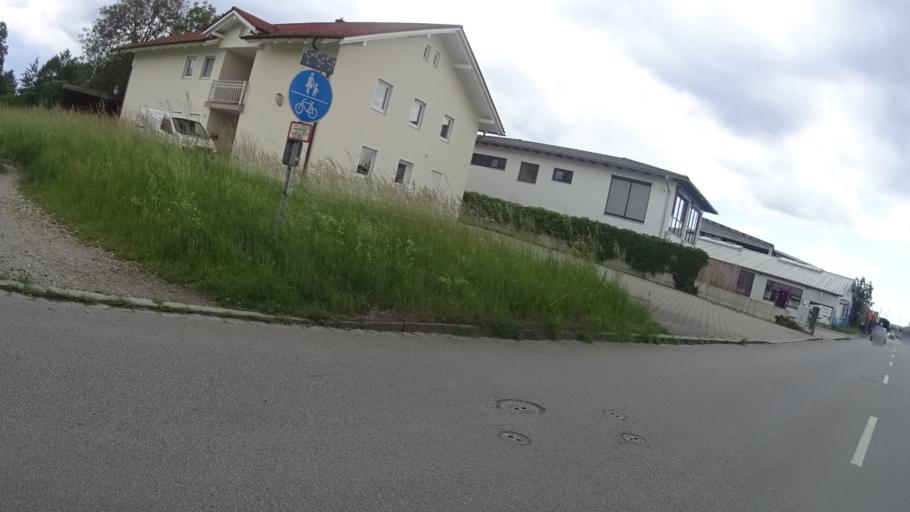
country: DE
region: Bavaria
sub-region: Lower Bavaria
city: Eggenfelden
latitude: 48.3998
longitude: 12.7583
